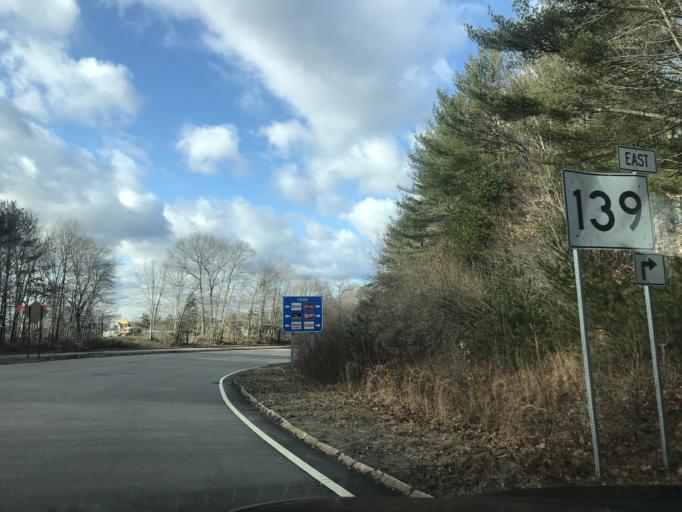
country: US
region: Massachusetts
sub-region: Plymouth County
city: North Pembroke
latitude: 42.1065
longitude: -70.7672
